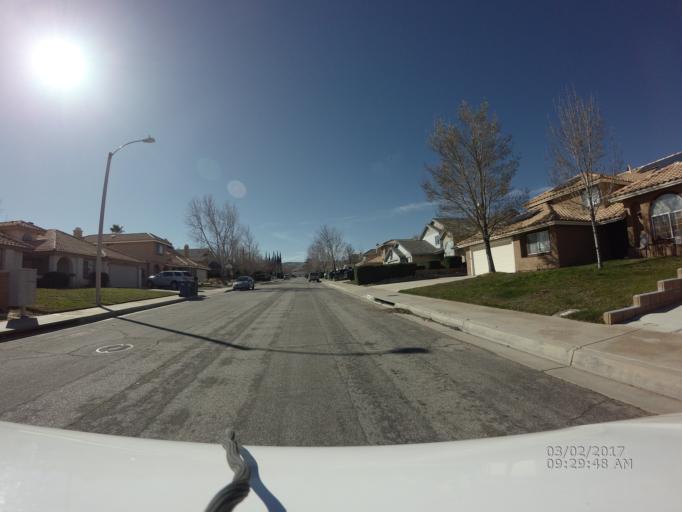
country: US
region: California
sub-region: Los Angeles County
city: Quartz Hill
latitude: 34.6373
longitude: -118.2215
